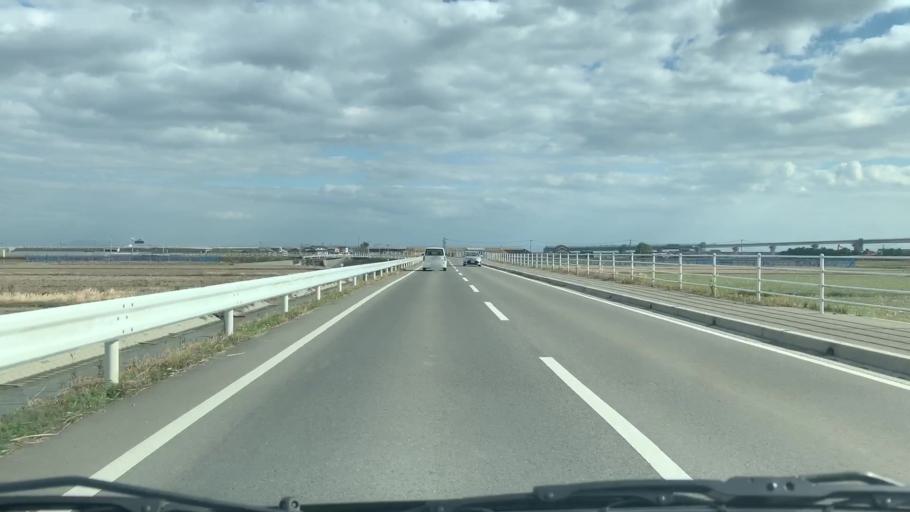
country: JP
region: Saga Prefecture
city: Saga-shi
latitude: 33.2027
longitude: 130.2070
